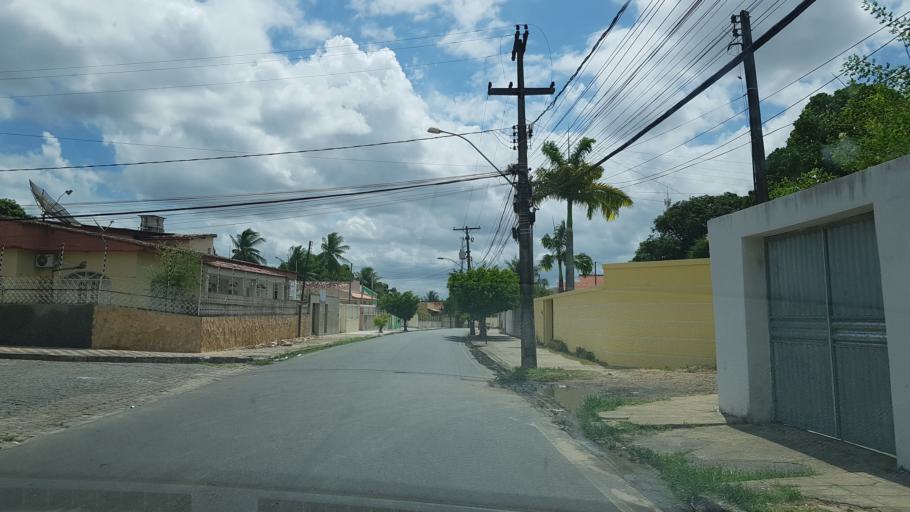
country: BR
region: Alagoas
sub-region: Penedo
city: Penedo
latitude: -10.2805
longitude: -36.5665
